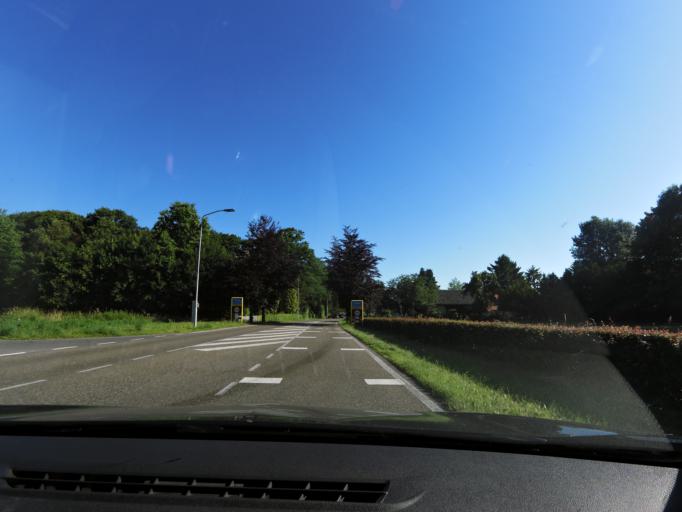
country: NL
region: Gelderland
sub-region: Gemeente Voorst
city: Twello
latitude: 52.2265
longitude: 6.1102
